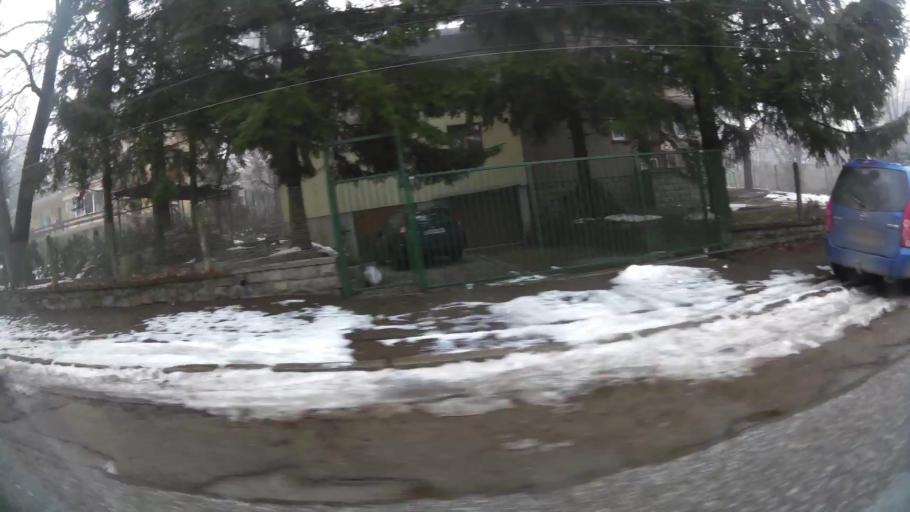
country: BG
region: Sofia-Capital
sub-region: Stolichna Obshtina
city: Sofia
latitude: 42.6590
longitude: 23.2515
